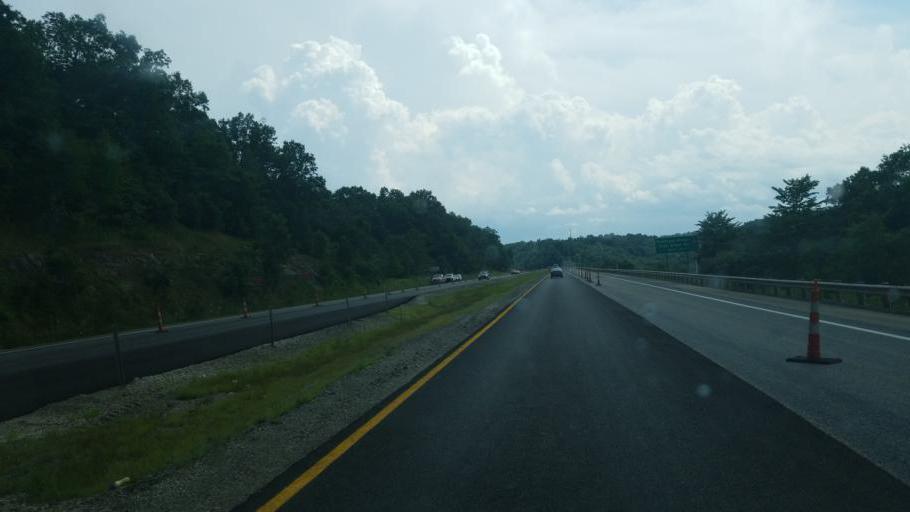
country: US
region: West Virginia
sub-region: Kanawha County
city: Alum Creek
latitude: 38.2430
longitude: -81.8380
